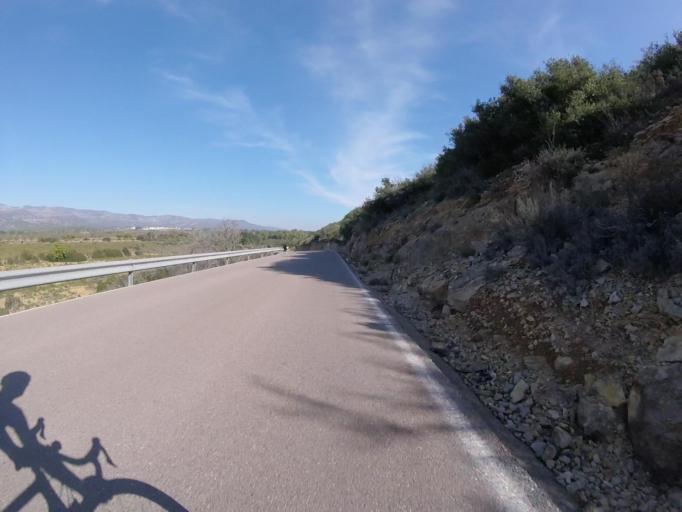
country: ES
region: Valencia
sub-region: Provincia de Castello
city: Benlloch
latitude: 40.2486
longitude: 0.0765
